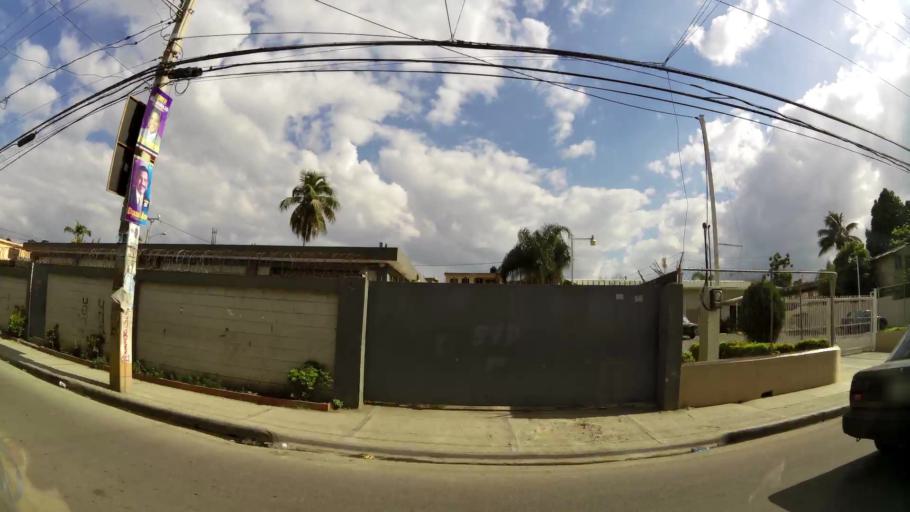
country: DO
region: Nacional
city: Ensanche Luperon
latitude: 18.5424
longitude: -69.8949
